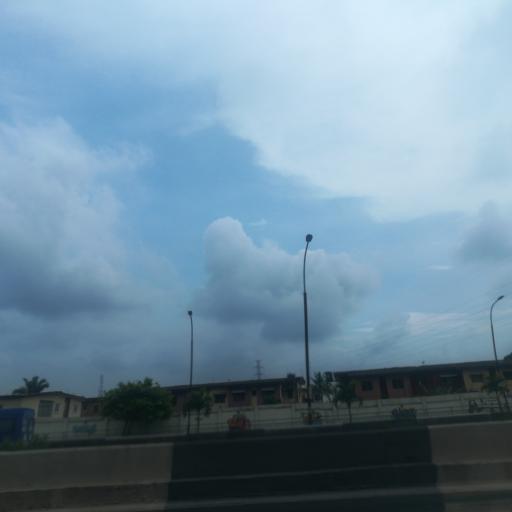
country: NG
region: Lagos
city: Ojota
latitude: 6.5824
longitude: 3.3920
